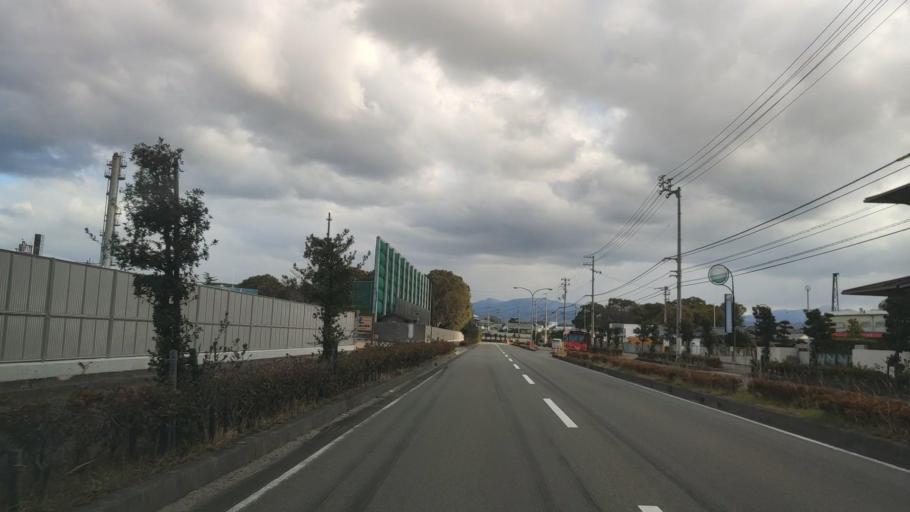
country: JP
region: Ehime
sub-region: Shikoku-chuo Shi
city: Matsuyama
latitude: 33.8463
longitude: 132.7106
